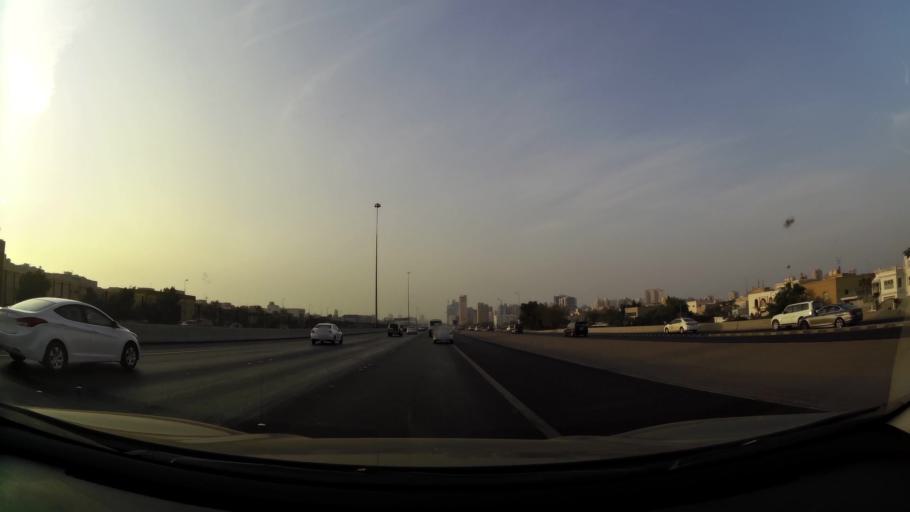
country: KW
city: Bayan
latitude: 29.3173
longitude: 48.0507
